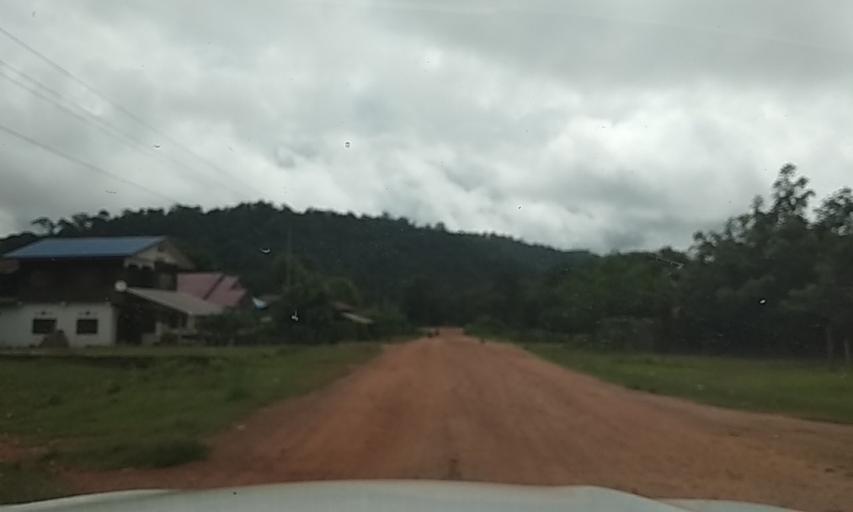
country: LA
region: Bolikhamxai
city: Bolikhan
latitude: 18.5571
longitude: 103.7397
